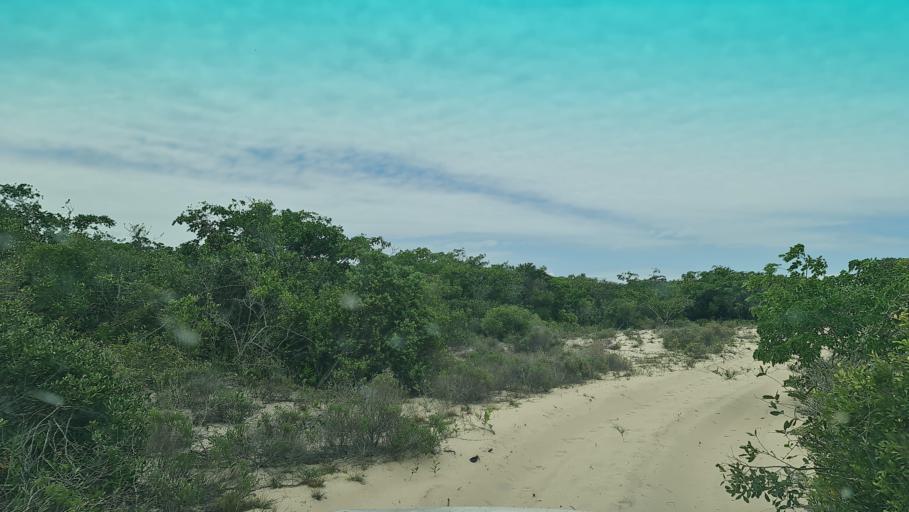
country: MZ
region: Maputo
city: Manhica
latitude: -25.6310
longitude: 32.7876
